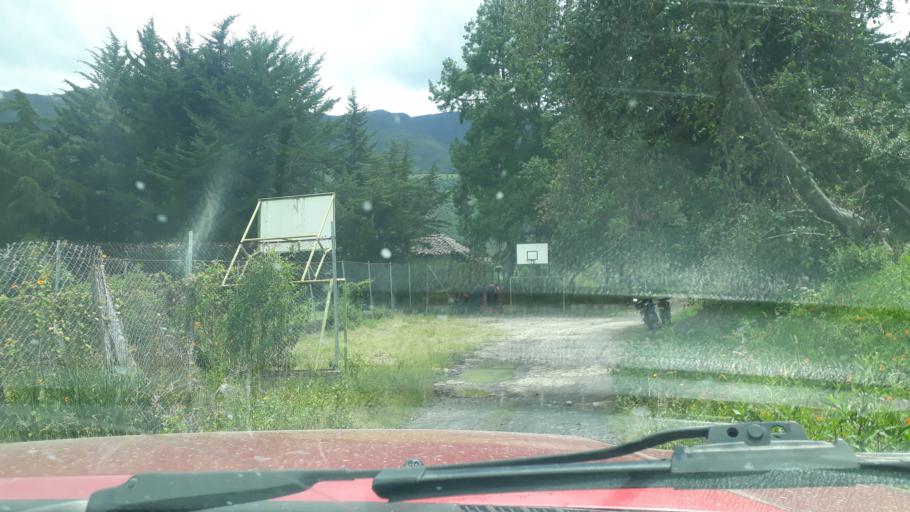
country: CO
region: Boyaca
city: San Mateo
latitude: 6.3908
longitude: -72.5364
